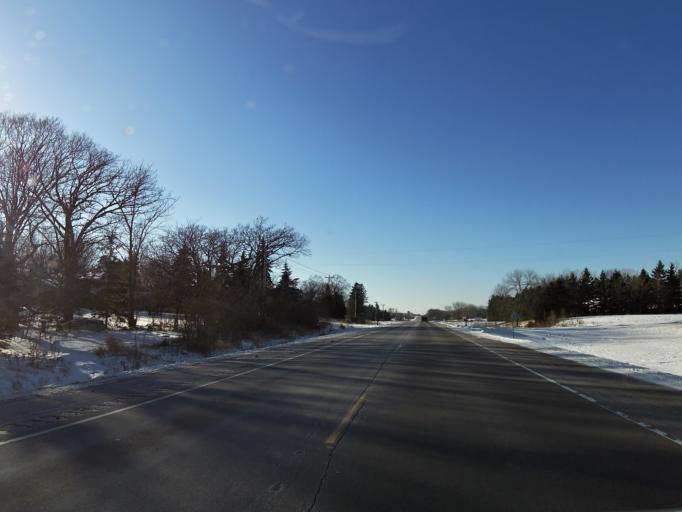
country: US
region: Minnesota
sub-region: Le Sueur County
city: New Prague
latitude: 44.5436
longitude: -93.5300
